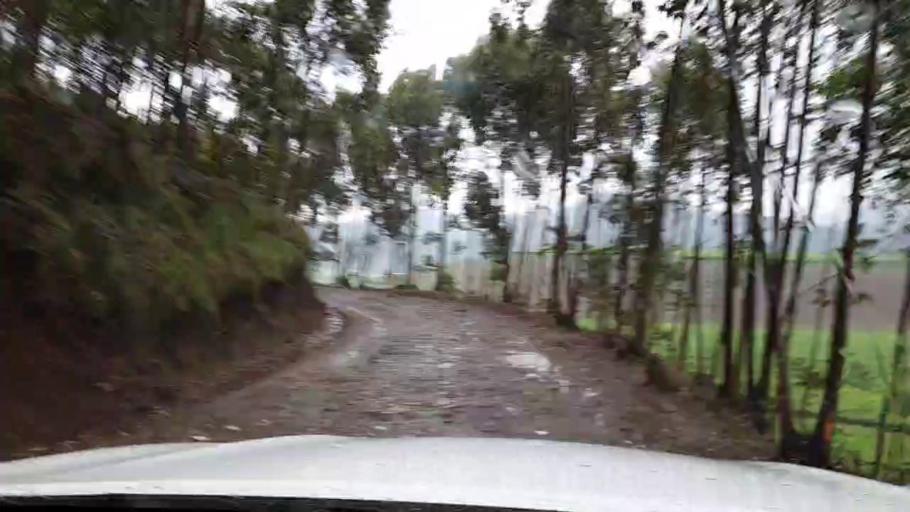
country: RW
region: Western Province
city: Cyangugu
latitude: -2.4697
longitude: 29.0335
